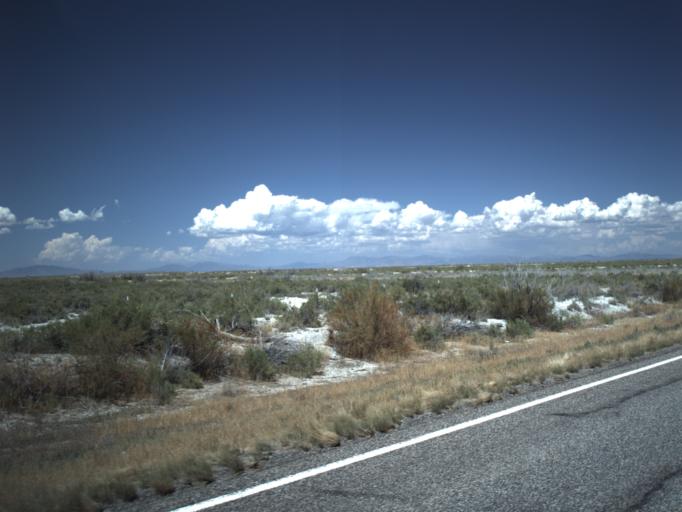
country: US
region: Utah
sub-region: Millard County
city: Delta
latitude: 39.2997
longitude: -112.8123
